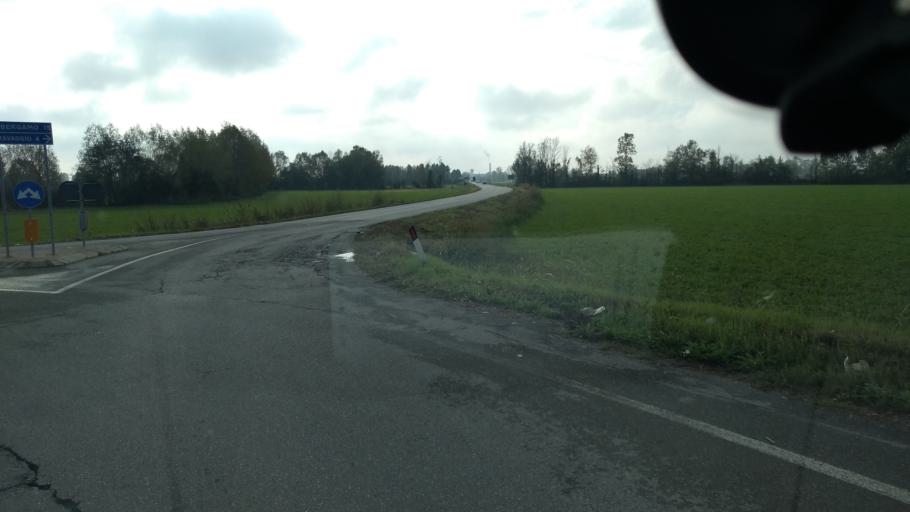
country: IT
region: Lombardy
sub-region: Provincia di Bergamo
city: Brignano Gera d'Adda
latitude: 45.5362
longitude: 9.6389
